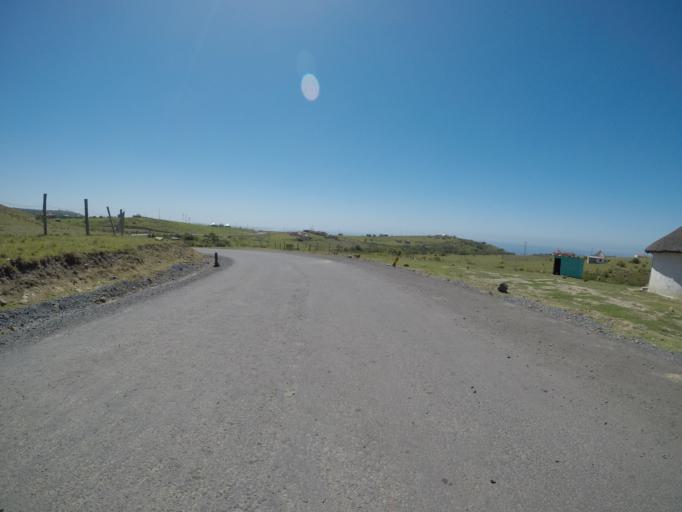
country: ZA
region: Eastern Cape
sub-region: OR Tambo District Municipality
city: Libode
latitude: -32.0004
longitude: 29.1194
